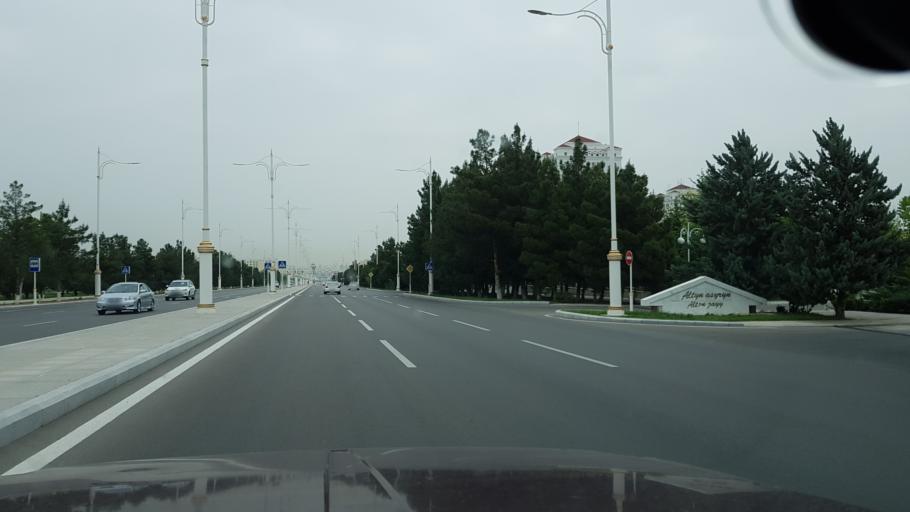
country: TM
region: Ahal
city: Ashgabat
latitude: 37.8879
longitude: 58.3878
